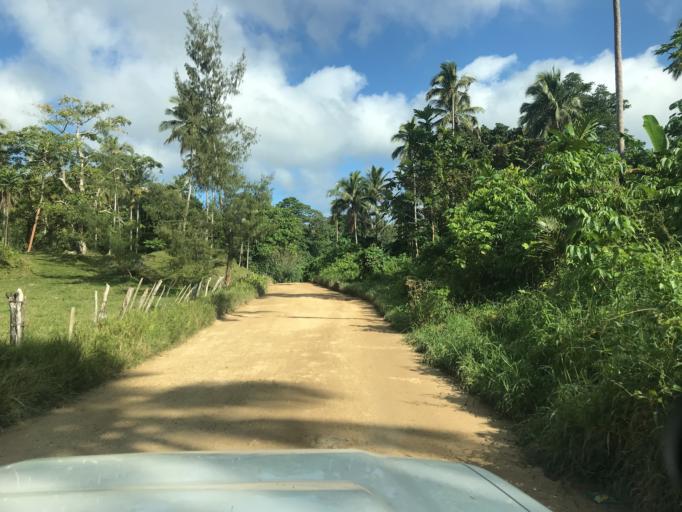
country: VU
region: Sanma
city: Luganville
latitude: -15.5058
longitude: 167.0994
